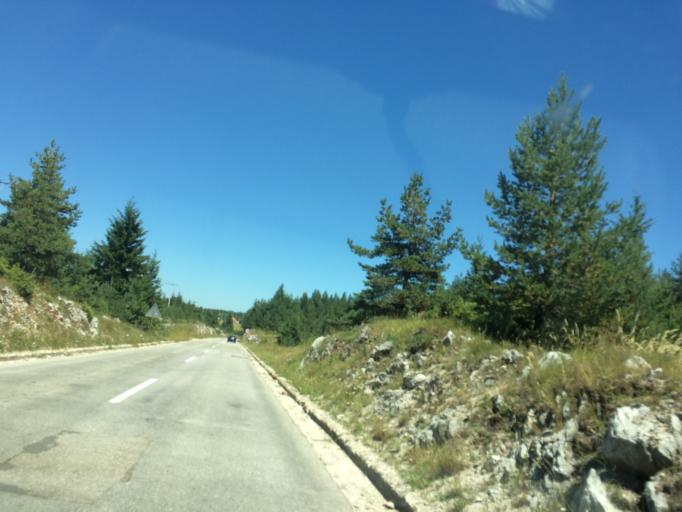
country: ME
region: Pljevlja
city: Pljevlja
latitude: 43.3387
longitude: 19.4793
